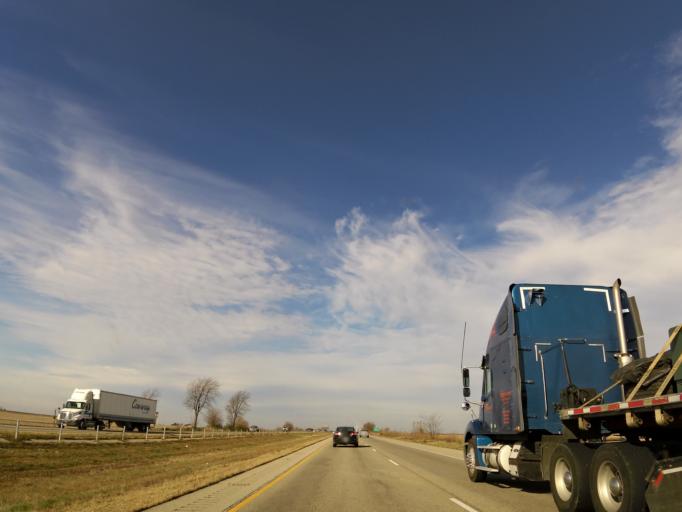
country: US
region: Illinois
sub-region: McLean County
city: Twin Grove
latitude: 40.5495
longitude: -89.0926
